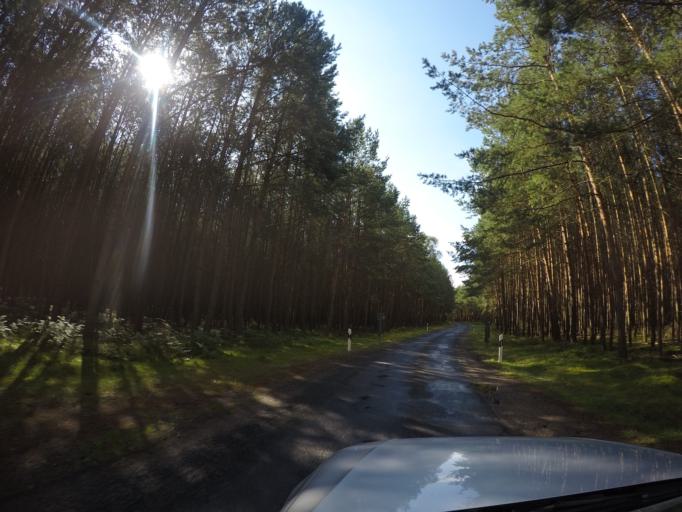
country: DE
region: Mecklenburg-Vorpommern
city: Wesenberg
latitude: 53.2805
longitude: 12.8867
